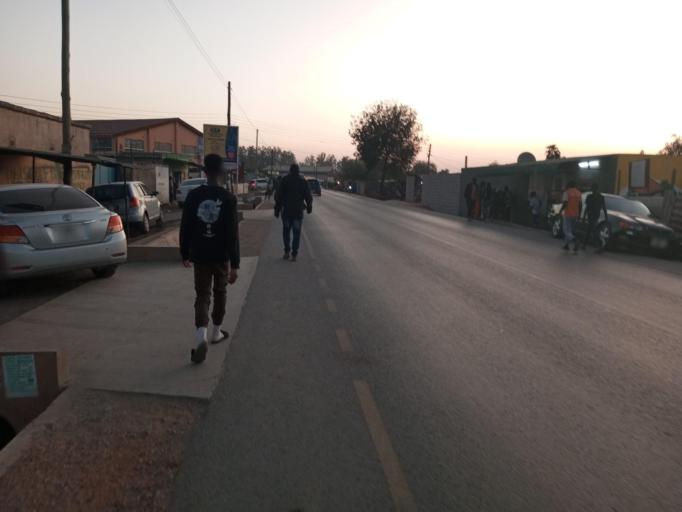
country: ZM
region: Lusaka
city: Lusaka
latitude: -15.3918
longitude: 28.2904
